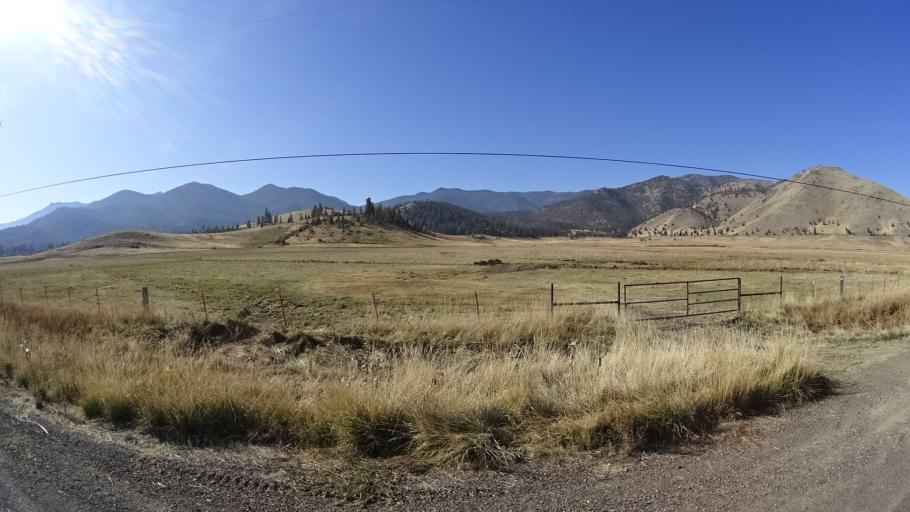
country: US
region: California
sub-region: Siskiyou County
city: Weed
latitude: 41.4538
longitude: -122.4576
